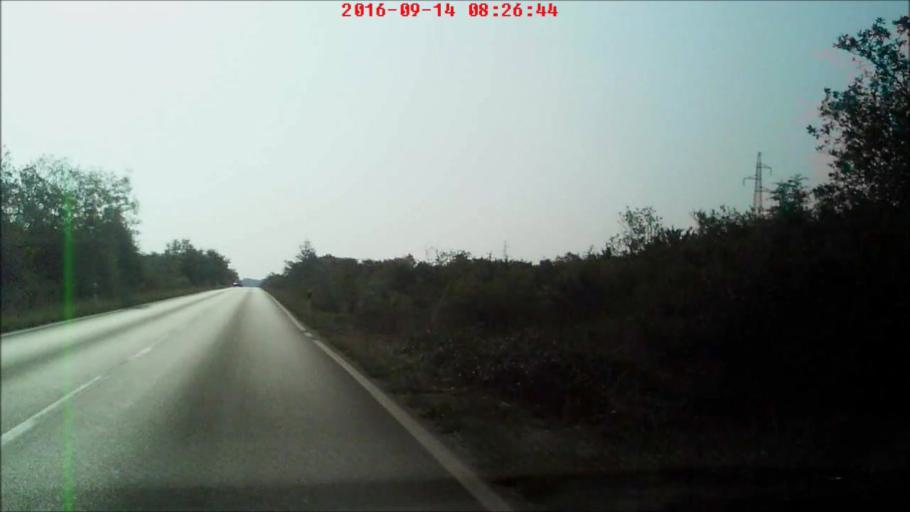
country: HR
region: Zadarska
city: Vrsi
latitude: 44.1936
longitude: 15.2573
